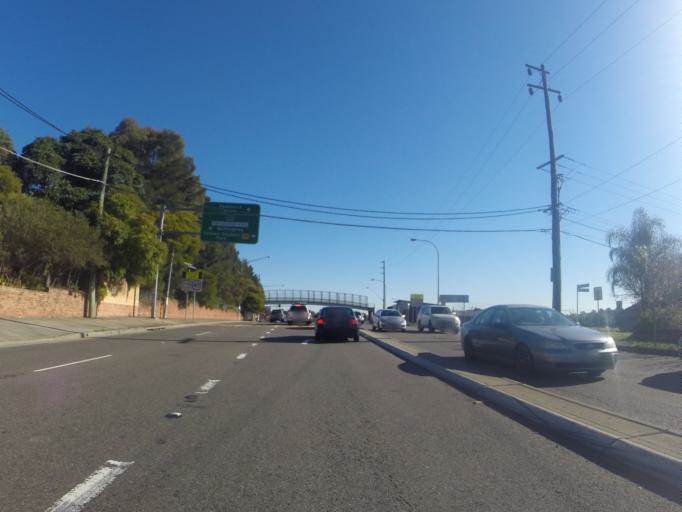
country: AU
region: New South Wales
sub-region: Hurstville
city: Penshurst
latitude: -33.9522
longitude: 151.0851
